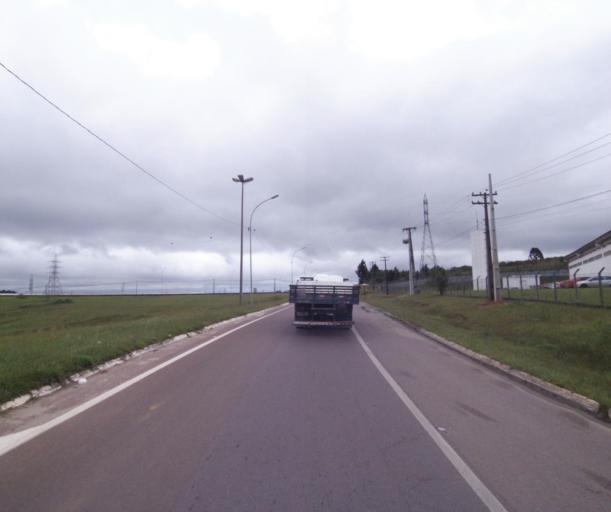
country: BR
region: Parana
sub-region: Quatro Barras
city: Quatro Barras
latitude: -25.3618
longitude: -49.0826
